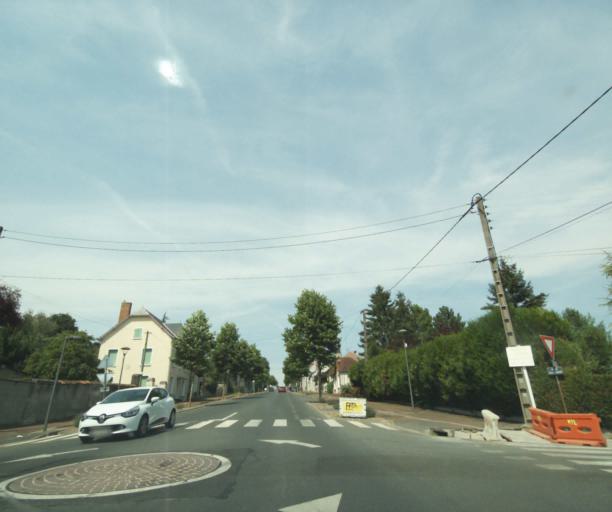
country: FR
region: Centre
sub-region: Departement d'Indre-et-Loire
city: Sainte-Maure-de-Touraine
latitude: 47.1140
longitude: 0.6178
